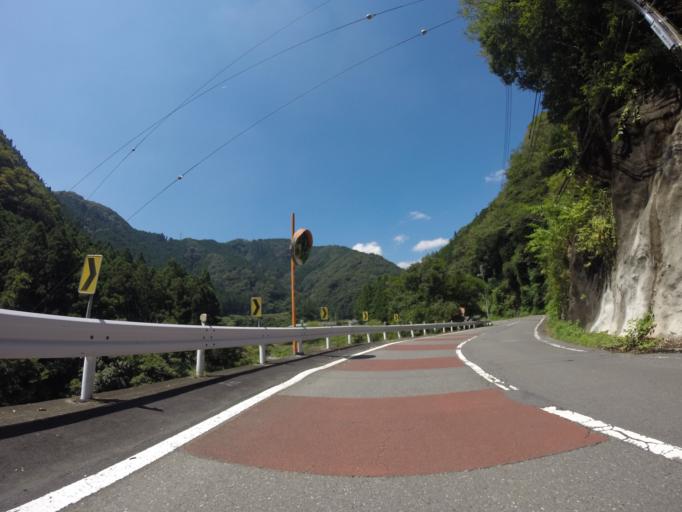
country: JP
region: Shizuoka
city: Shizuoka-shi
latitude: 35.0412
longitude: 138.2530
